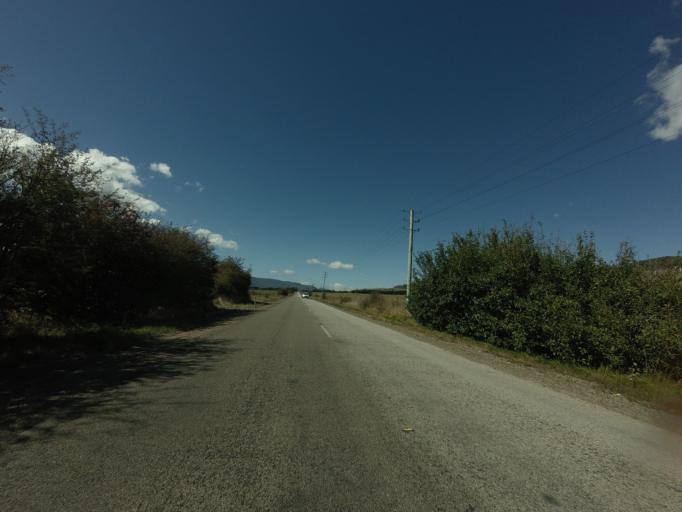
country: AU
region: Tasmania
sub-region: Break O'Day
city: St Helens
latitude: -41.6233
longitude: 147.9976
